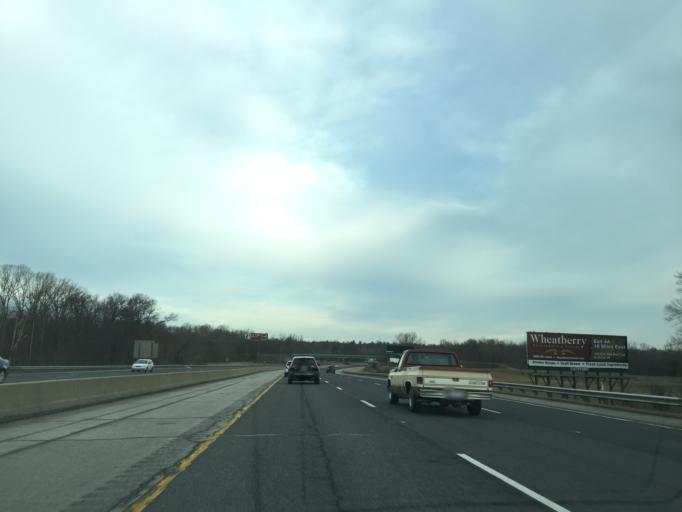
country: US
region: Indiana
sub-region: LaPorte County
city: Long Beach
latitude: 41.7196
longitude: -86.8057
